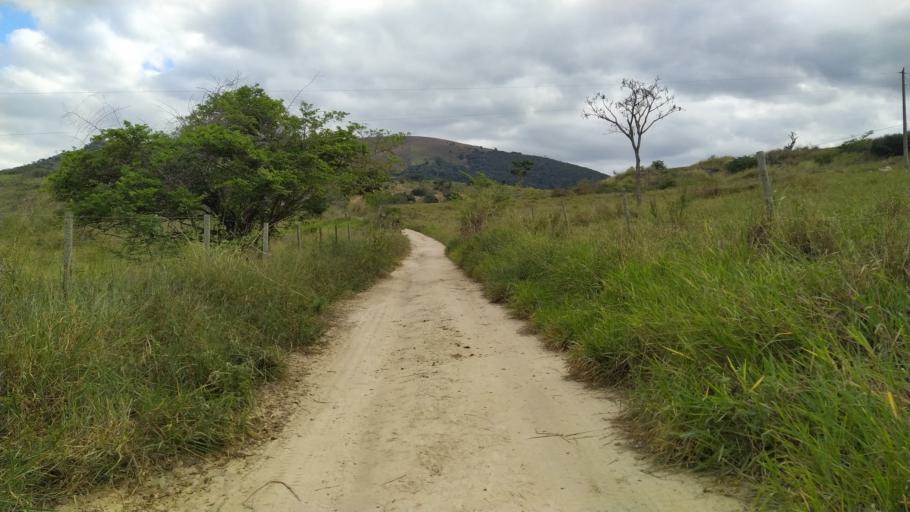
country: BR
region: Minas Gerais
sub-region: Almenara
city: Almenara
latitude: -16.6293
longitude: -40.4583
